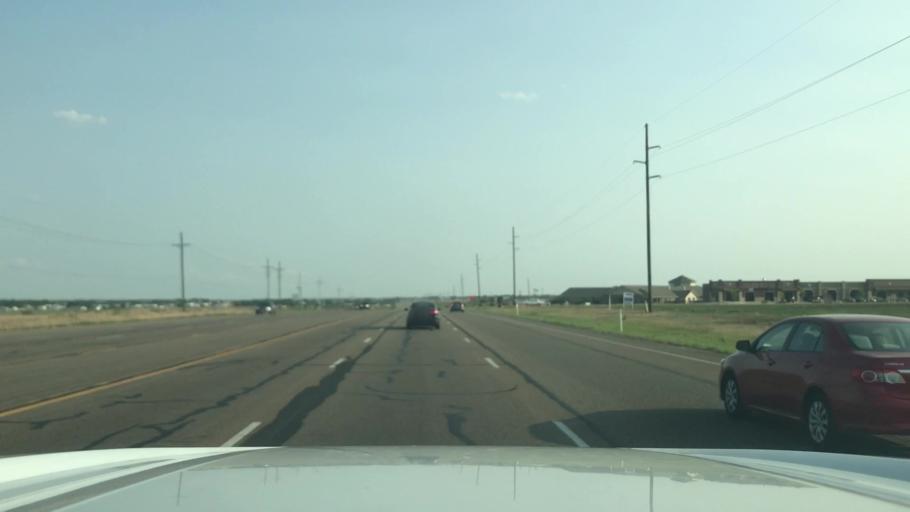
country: US
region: Texas
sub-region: Potter County
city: Amarillo
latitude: 35.1428
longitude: -101.9382
